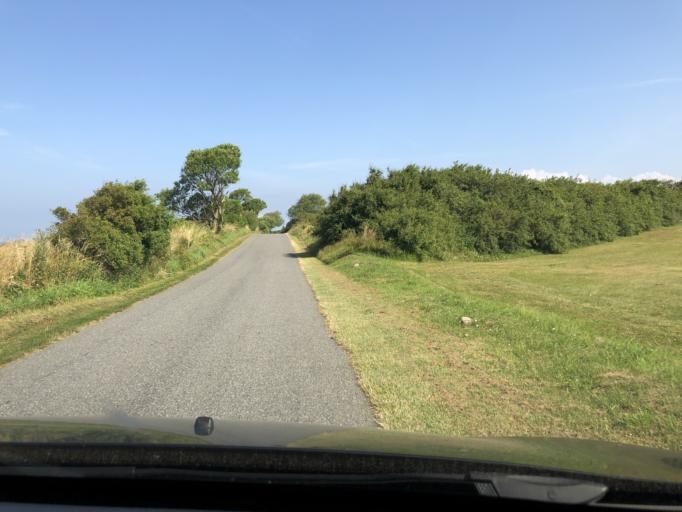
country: DK
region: South Denmark
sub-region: Faaborg-Midtfyn Kommune
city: Faaborg
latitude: 54.9629
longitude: 10.2124
